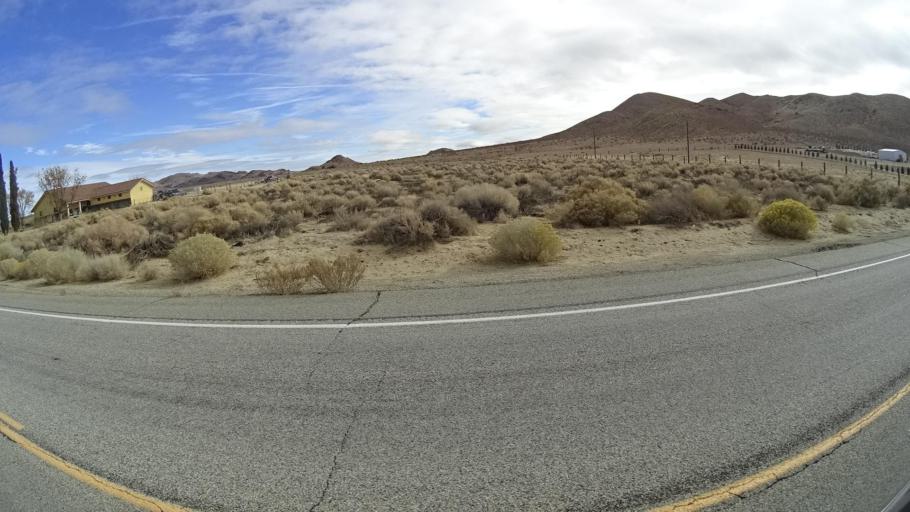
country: US
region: California
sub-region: Kern County
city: Rosamond
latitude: 34.8897
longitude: -118.2911
